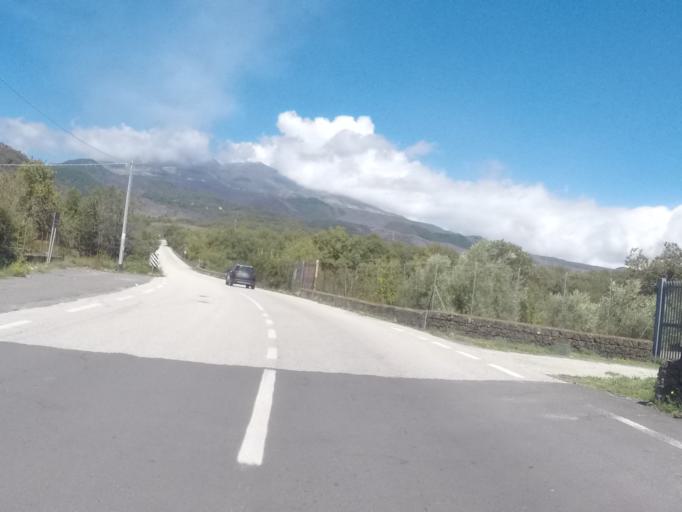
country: IT
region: Sicily
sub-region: Catania
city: Ragalna
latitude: 37.6457
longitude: 14.9879
